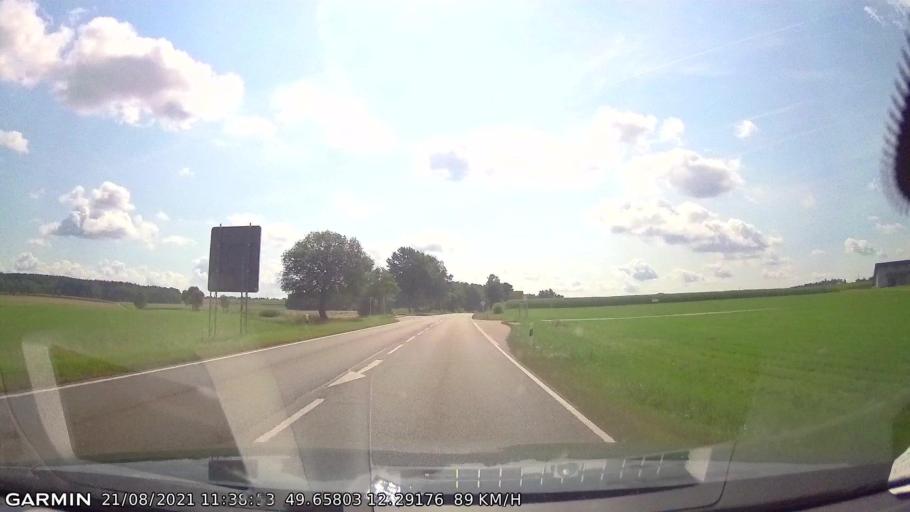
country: DE
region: Bavaria
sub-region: Upper Palatinate
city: Waldthurn
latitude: 49.6580
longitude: 12.2917
